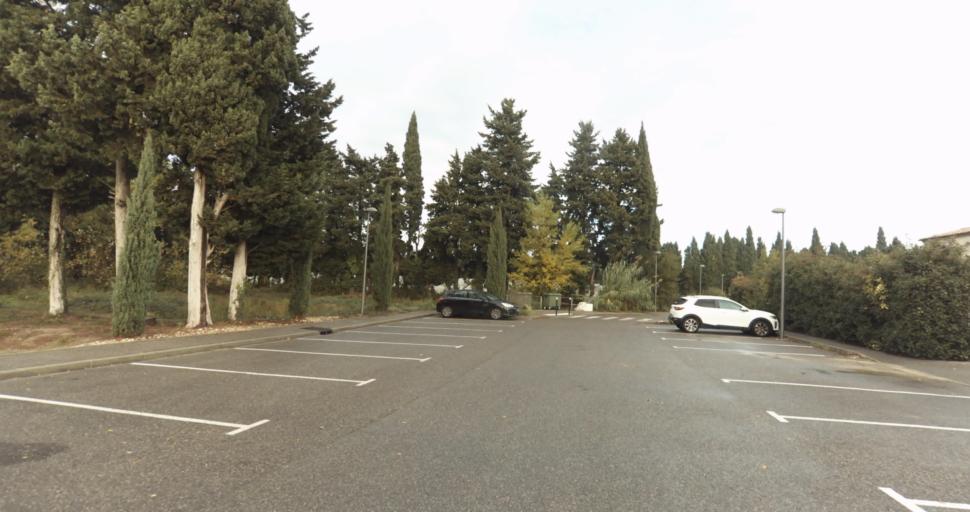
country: FR
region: Provence-Alpes-Cote d'Azur
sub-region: Departement des Bouches-du-Rhone
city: Rognonas
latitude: 43.8983
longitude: 4.7958
